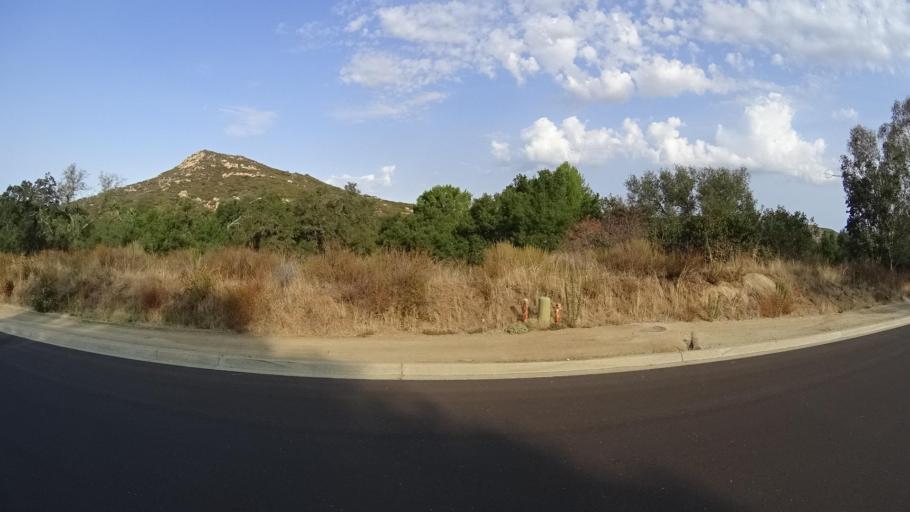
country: US
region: California
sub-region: San Diego County
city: San Diego Country Estates
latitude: 33.0056
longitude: -116.7960
